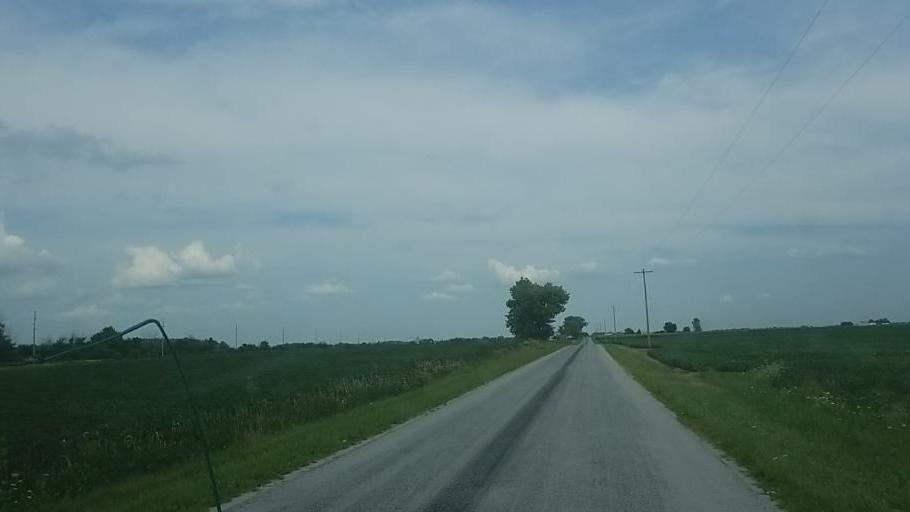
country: US
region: Ohio
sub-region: Wyandot County
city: Upper Sandusky
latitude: 40.8178
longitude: -83.3479
